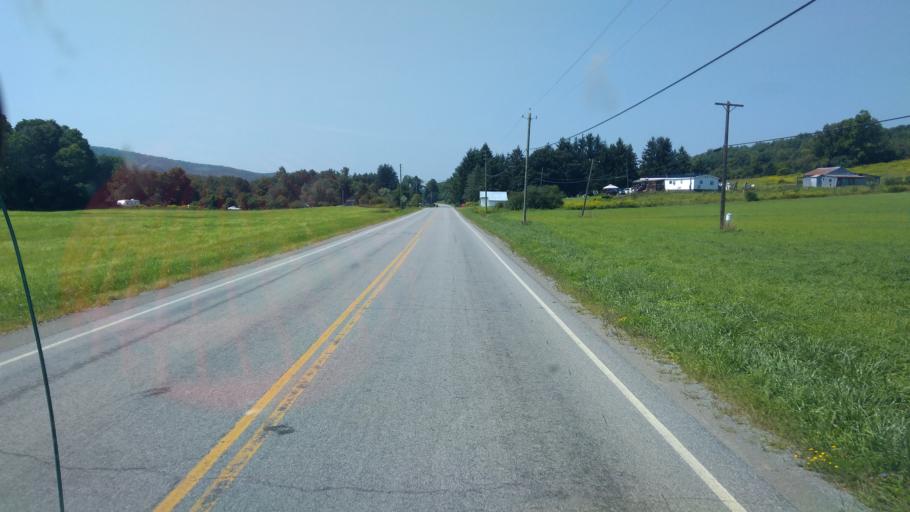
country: US
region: New York
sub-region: Allegany County
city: Belmont
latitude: 42.3028
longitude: -77.9772
